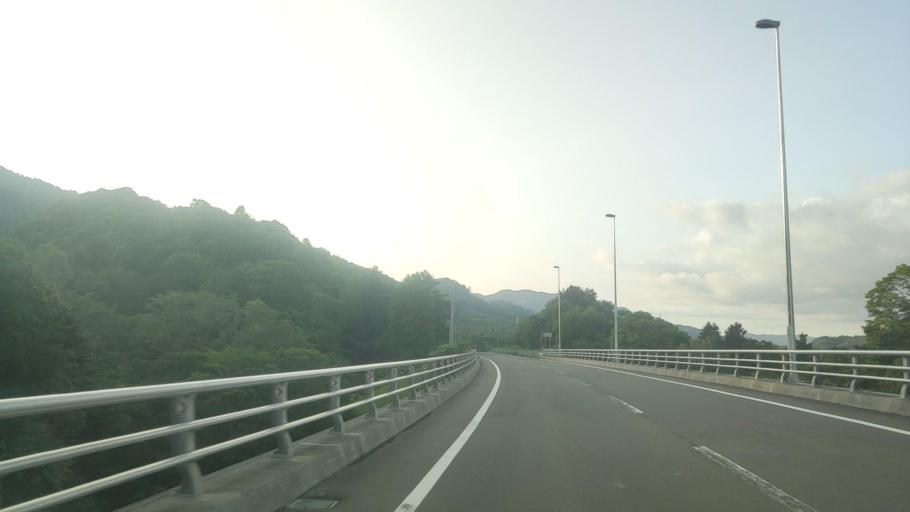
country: JP
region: Hokkaido
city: Bibai
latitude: 43.0786
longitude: 142.1014
